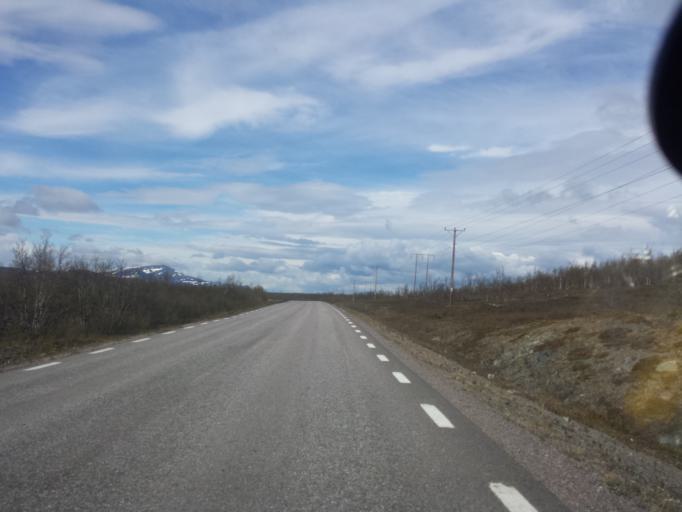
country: SE
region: Norrbotten
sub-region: Kiruna Kommun
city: Kiruna
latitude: 68.0474
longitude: 19.8305
